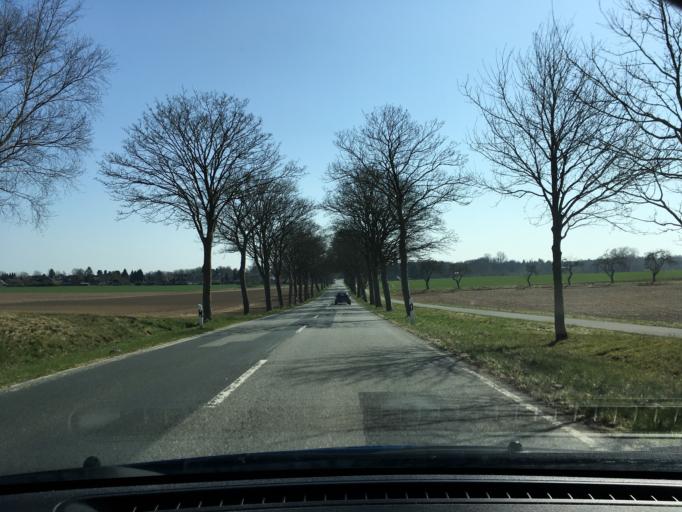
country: DE
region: Lower Saxony
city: Wriedel
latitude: 53.0408
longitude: 10.2969
